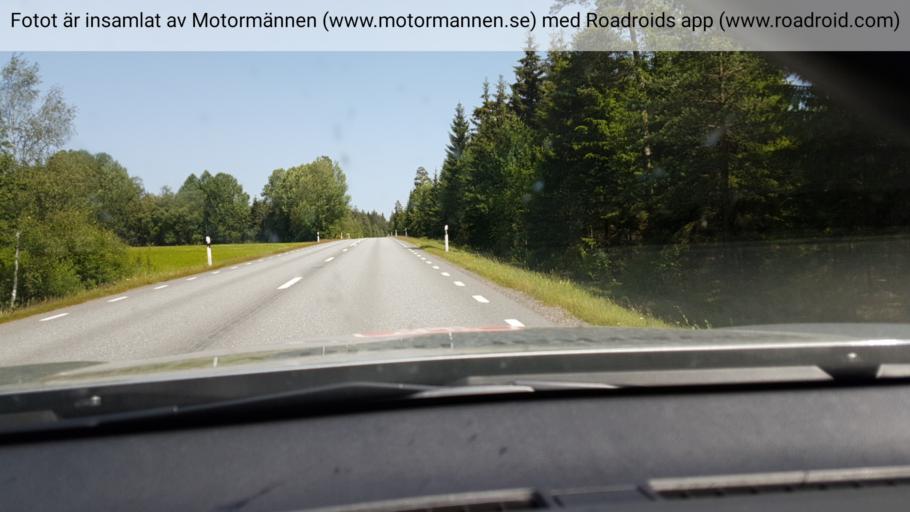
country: SE
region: Joenkoeping
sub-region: Nassjo Kommun
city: Bodafors
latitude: 57.4508
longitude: 14.7238
